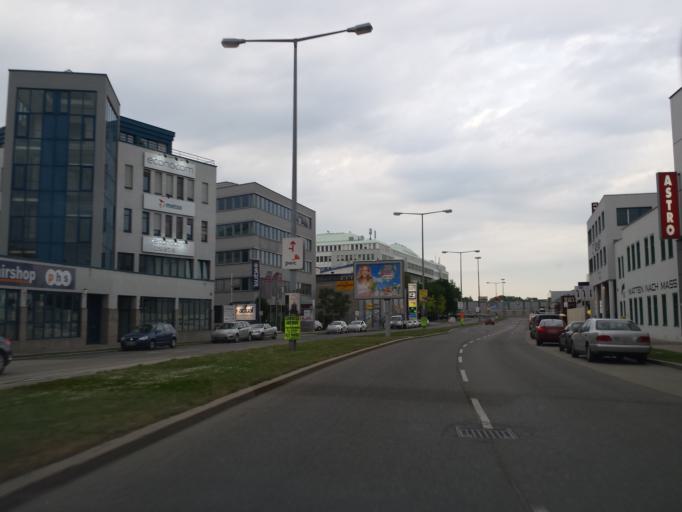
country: AT
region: Vienna
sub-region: Wien Stadt
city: Vienna
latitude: 48.1879
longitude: 16.4140
